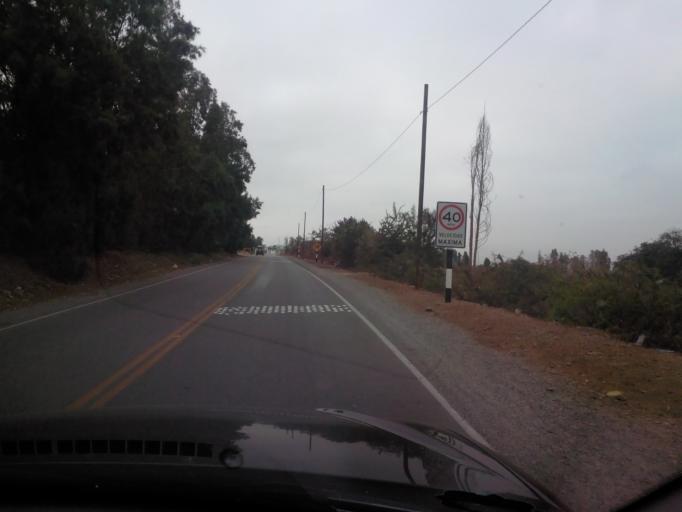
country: PE
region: Ica
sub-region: Provincia de Pisco
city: Humay
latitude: -13.7257
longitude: -75.9472
